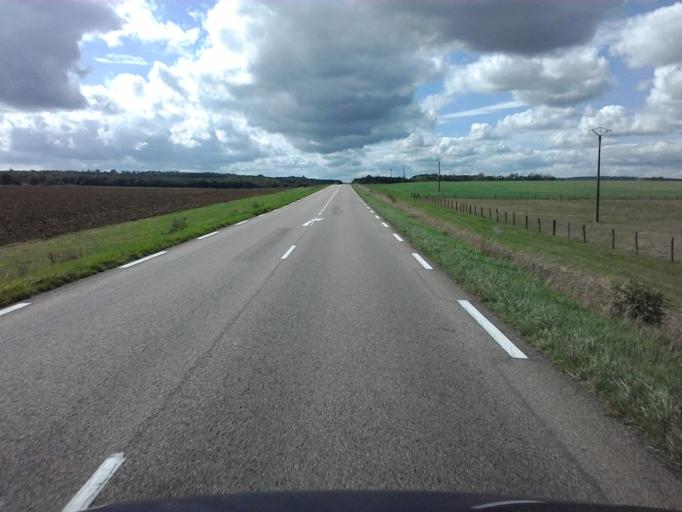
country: FR
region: Lorraine
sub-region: Departement de Meurthe-et-Moselle
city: Colombey-les-Belles
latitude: 48.4694
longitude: 5.8295
